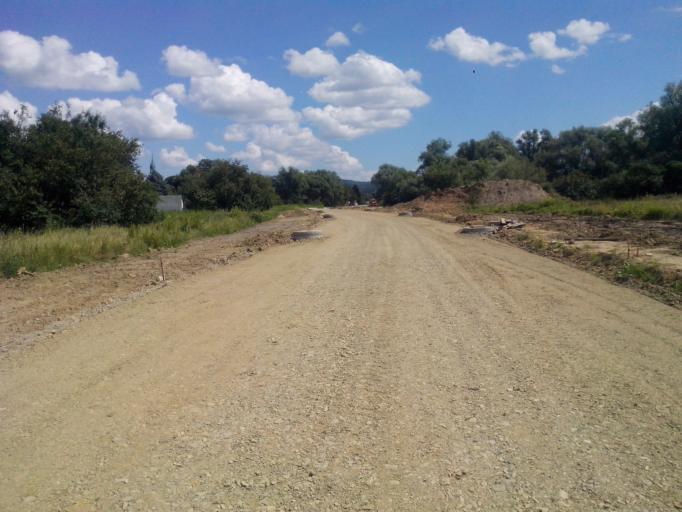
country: PL
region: Subcarpathian Voivodeship
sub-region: Powiat strzyzowski
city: Strzyzow
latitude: 49.8682
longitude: 21.7778
